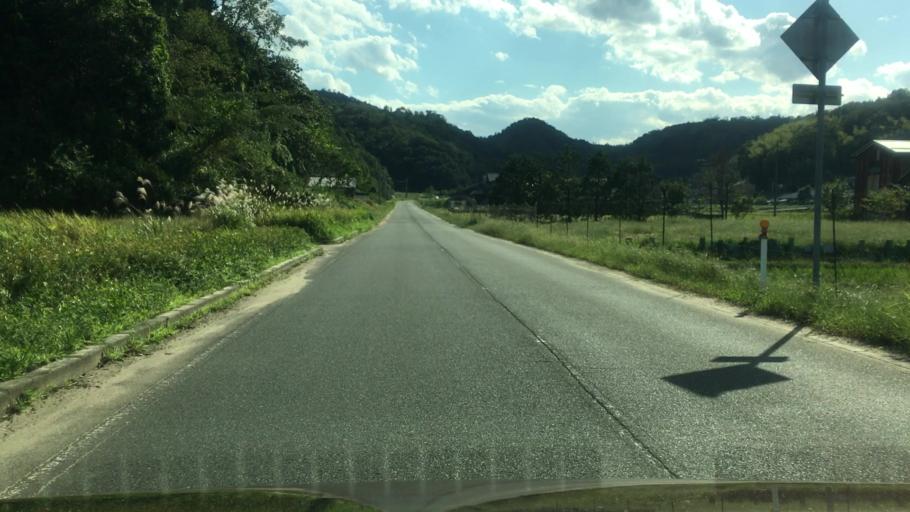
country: JP
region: Hyogo
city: Toyooka
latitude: 35.6498
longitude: 134.9662
